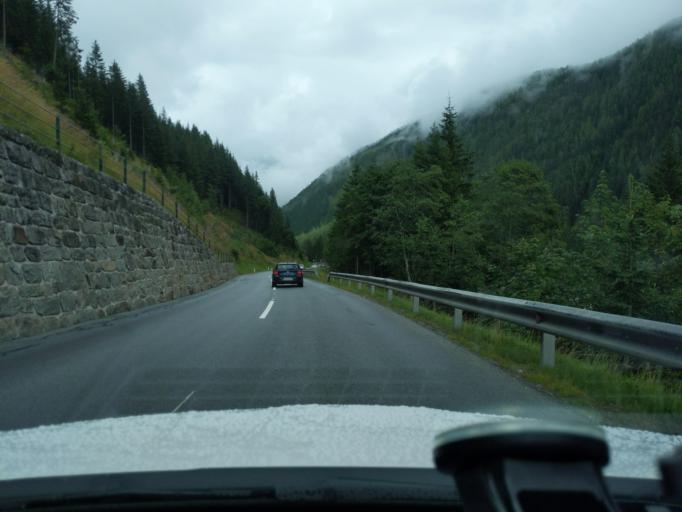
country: AT
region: Tyrol
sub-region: Politischer Bezirk Innsbruck Land
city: Schmirn
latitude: 47.1191
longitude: 11.6886
